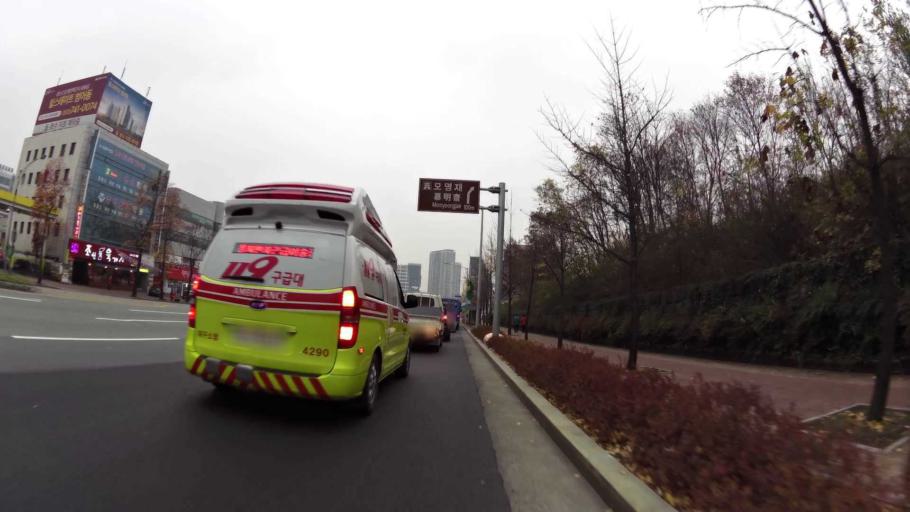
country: KR
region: Daegu
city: Daegu
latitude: 35.8552
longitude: 128.6533
